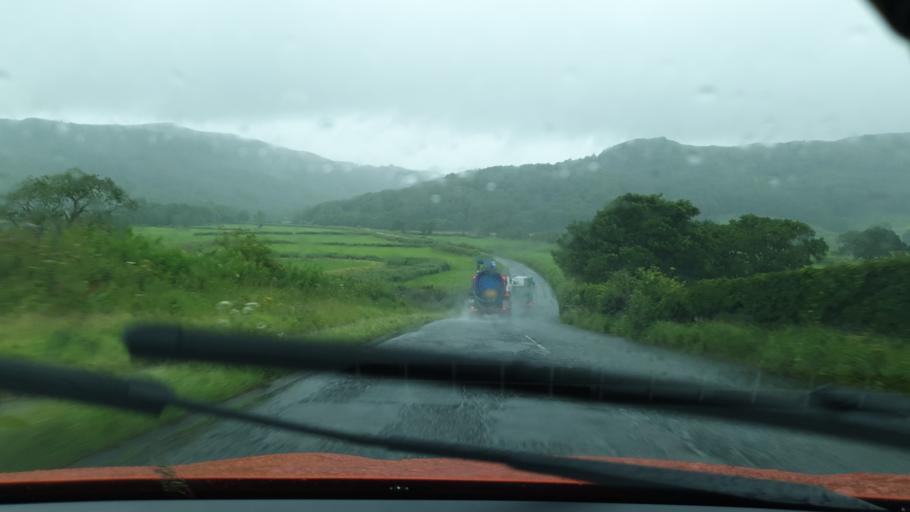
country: GB
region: England
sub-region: Cumbria
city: Millom
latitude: 54.2801
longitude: -3.2204
